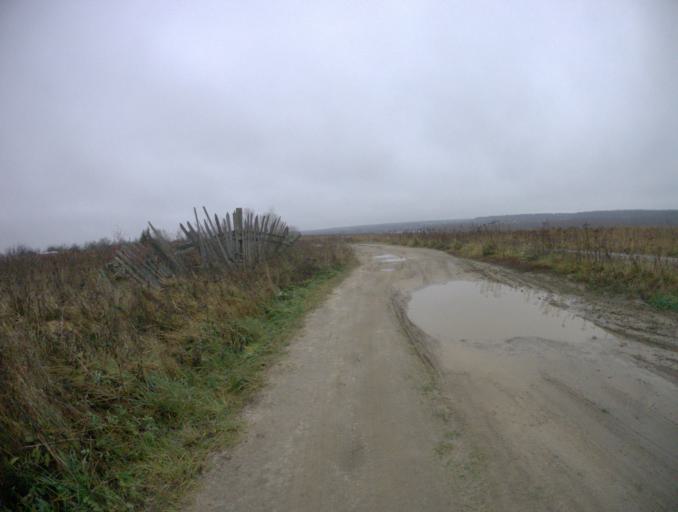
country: RU
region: Vladimir
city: Golovino
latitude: 55.9816
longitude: 40.4480
